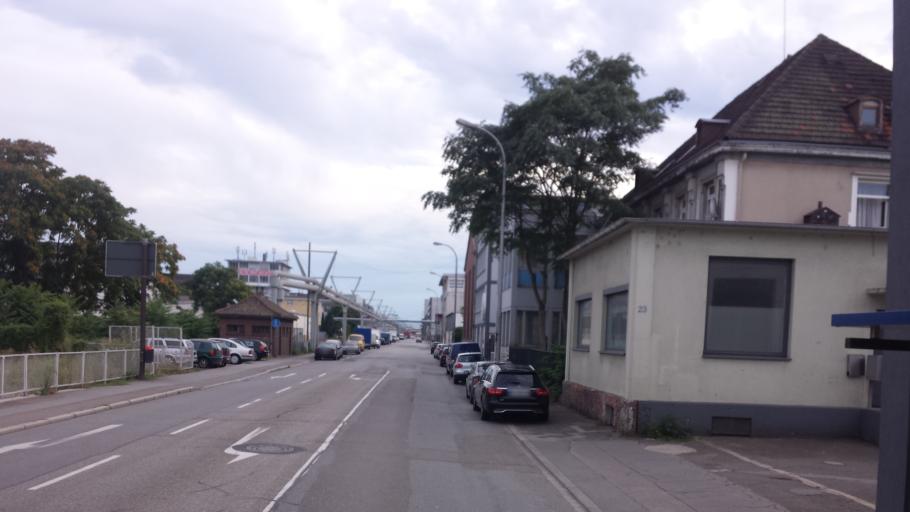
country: DE
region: Baden-Wuerttemberg
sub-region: Karlsruhe Region
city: Mannheim
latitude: 49.5179
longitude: 8.4630
